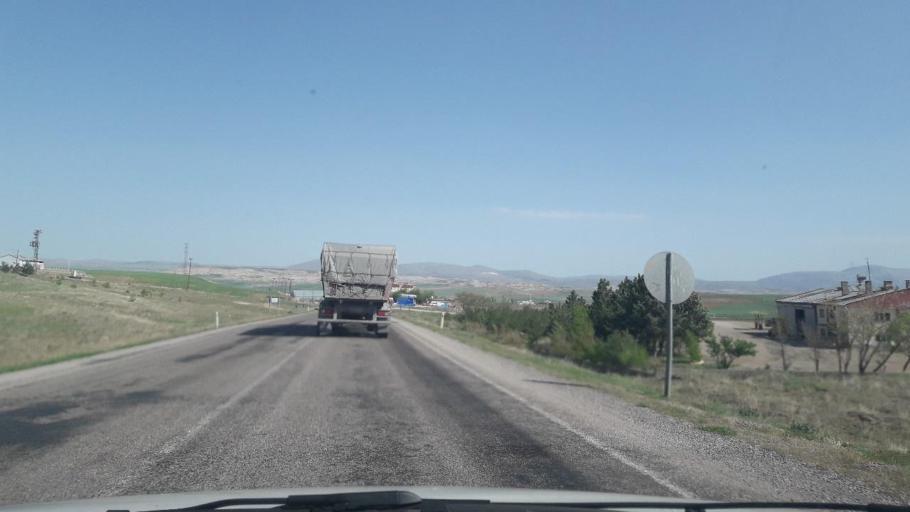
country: TR
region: Sivas
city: Kangal
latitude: 39.2163
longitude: 37.4082
